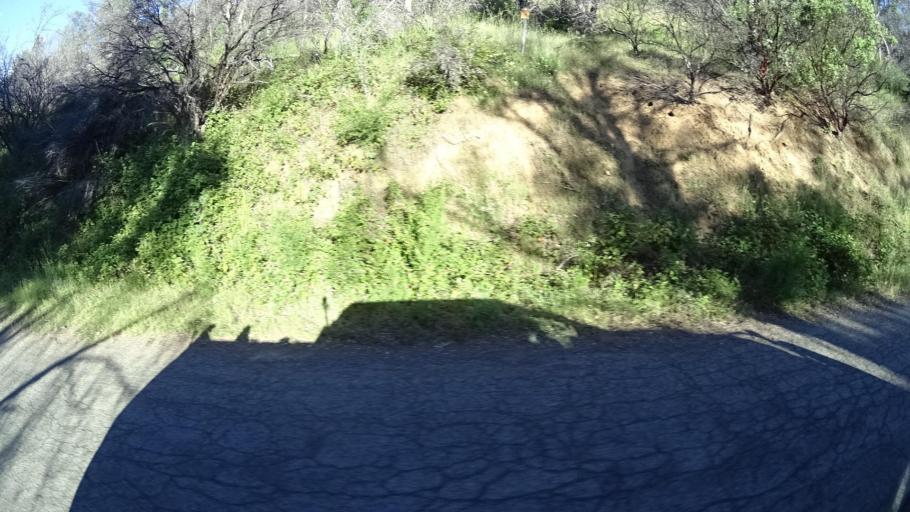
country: US
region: California
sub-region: Lake County
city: Upper Lake
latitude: 39.2677
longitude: -122.9287
